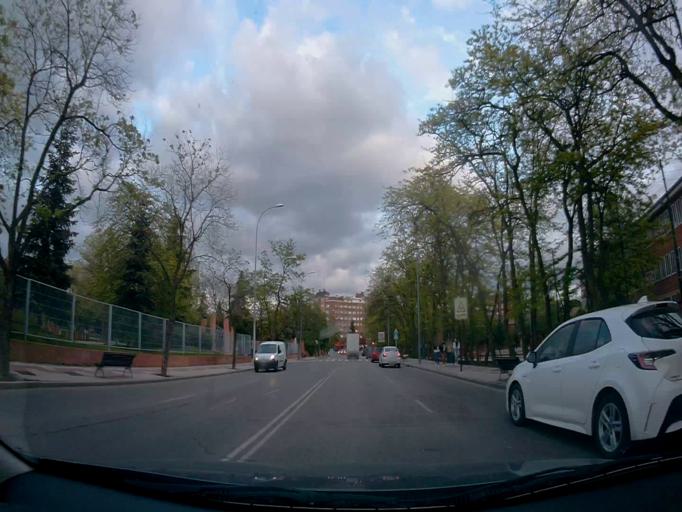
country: ES
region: Madrid
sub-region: Provincia de Madrid
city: Alcorcon
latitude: 40.3405
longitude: -3.8394
